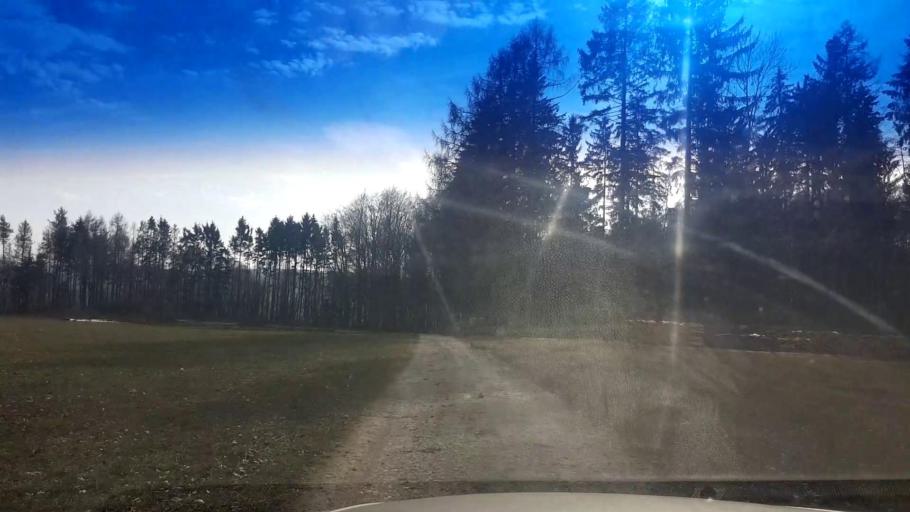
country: DE
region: Bavaria
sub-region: Upper Franconia
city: Litzendorf
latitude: 49.9291
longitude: 11.0619
